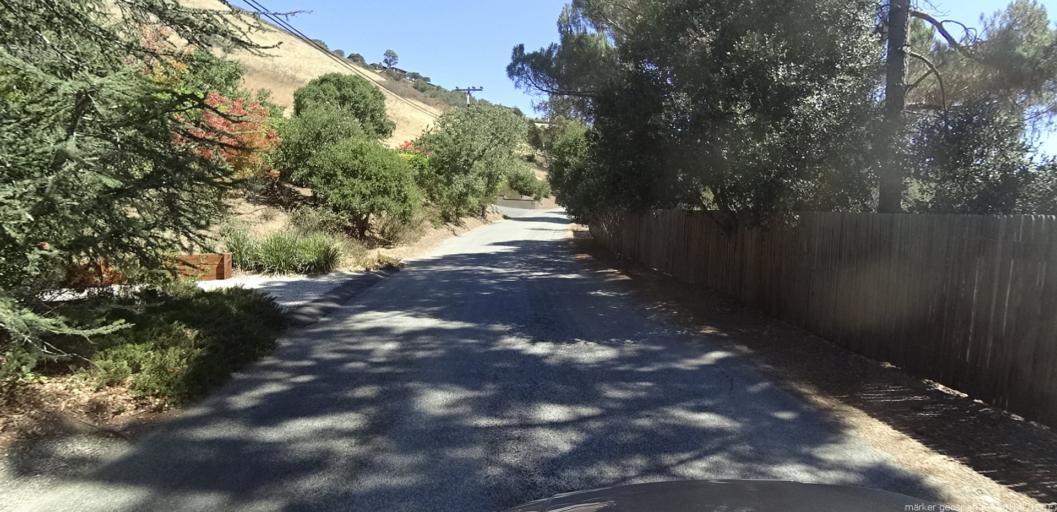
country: US
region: California
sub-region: Monterey County
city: Carmel Valley Village
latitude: 36.4960
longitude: -121.7444
